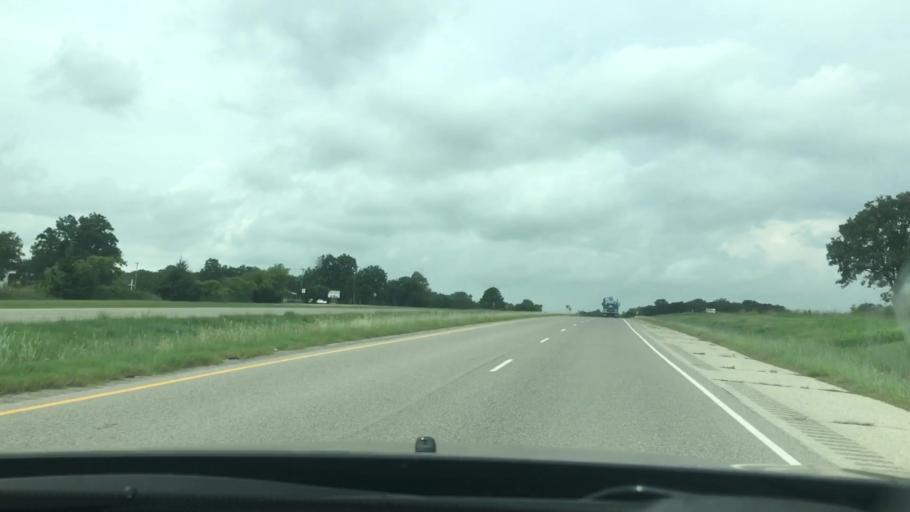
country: US
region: Oklahoma
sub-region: Carter County
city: Wilson
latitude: 34.1731
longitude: -97.4236
